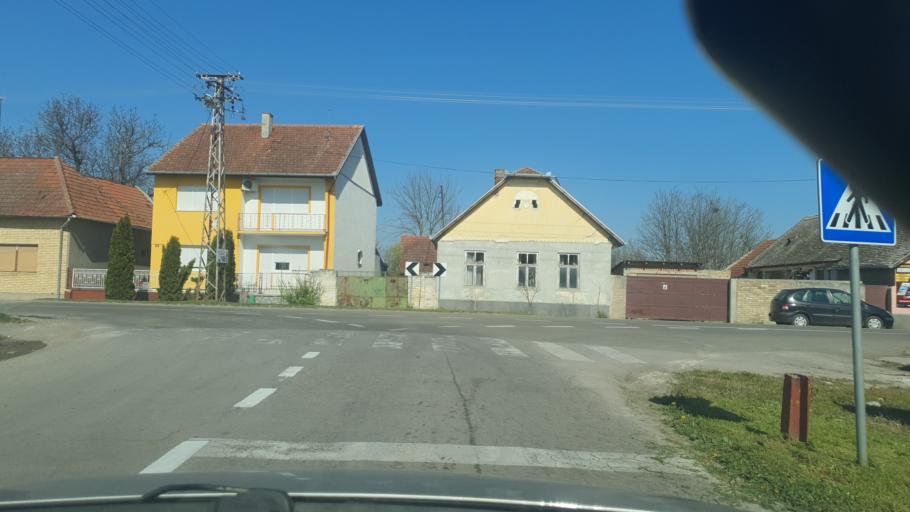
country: RS
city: Kolut
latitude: 45.8597
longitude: 18.9292
